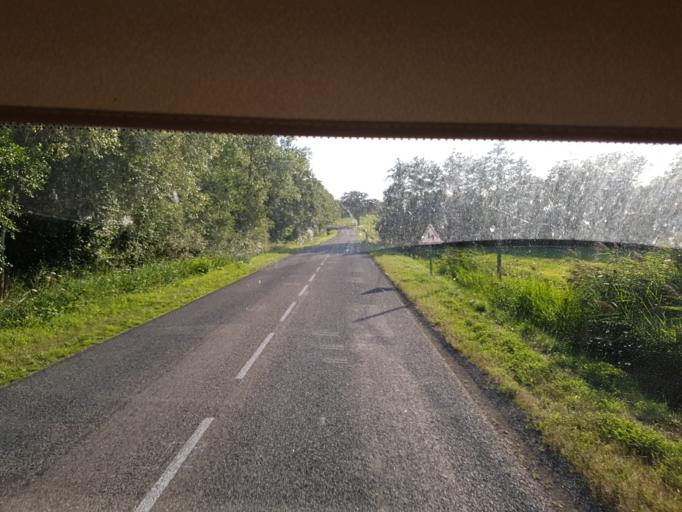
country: FR
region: Rhone-Alpes
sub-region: Departement de l'Ain
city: Chalamont
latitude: 46.0172
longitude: 5.2080
